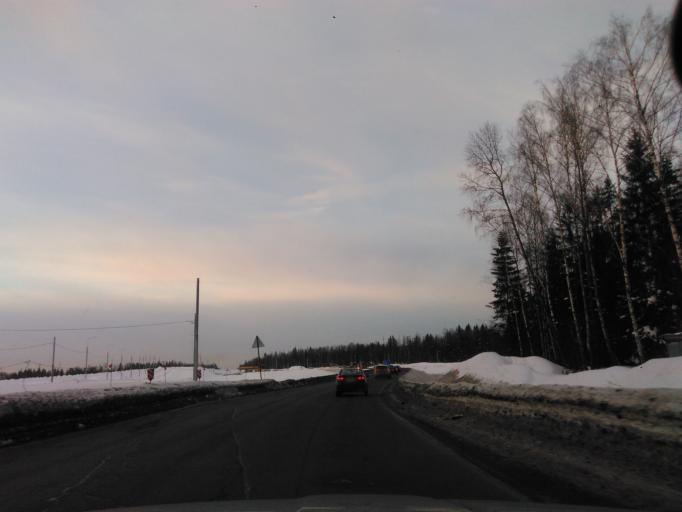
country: RU
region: Moskovskaya
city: Povarovo
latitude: 56.0103
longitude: 37.0274
